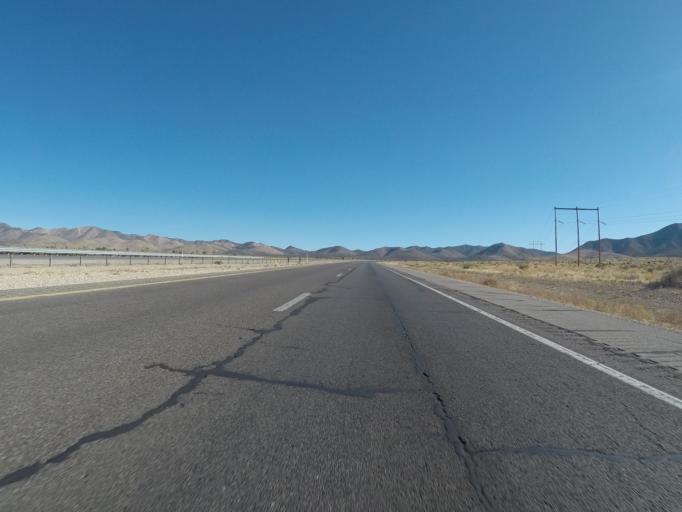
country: US
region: Nevada
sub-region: Clark County
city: Sandy Valley
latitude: 36.0203
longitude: -115.5563
